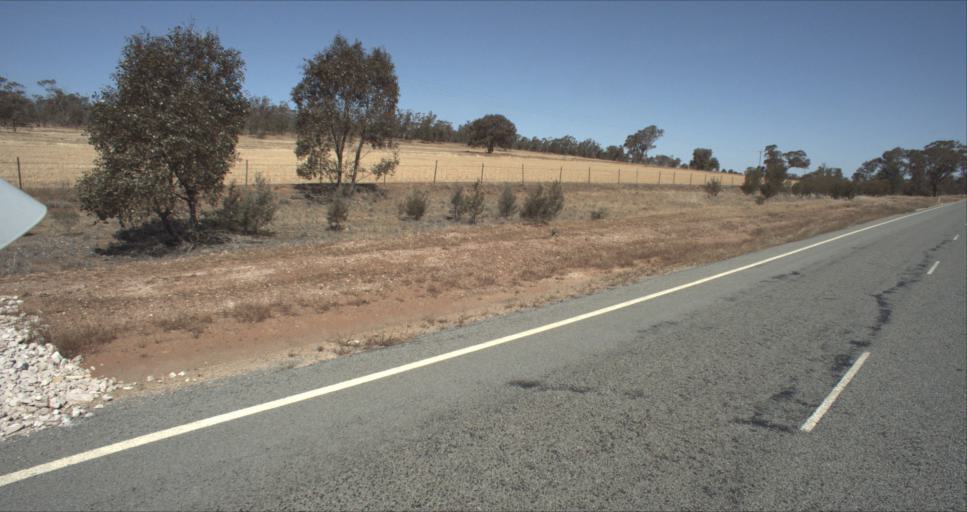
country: AU
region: New South Wales
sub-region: Leeton
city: Leeton
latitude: -34.4755
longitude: 146.4352
